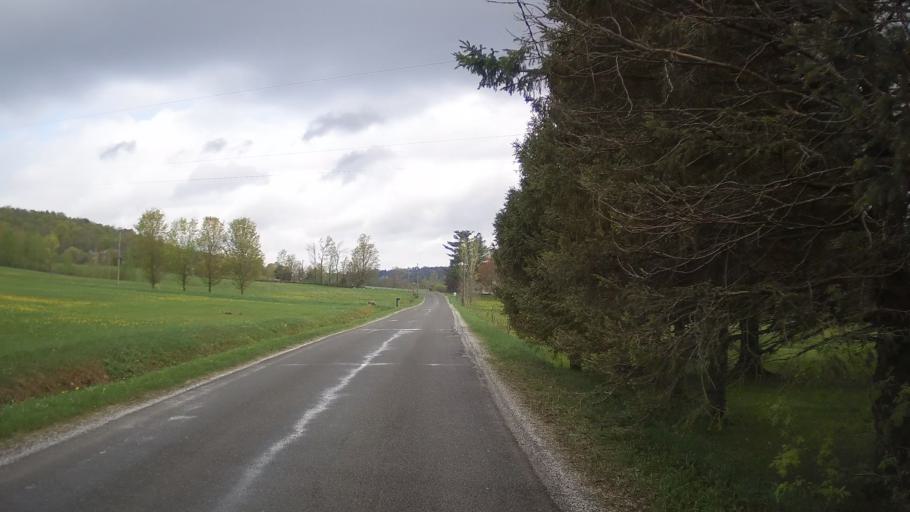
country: CA
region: Quebec
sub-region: Monteregie
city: Cowansville
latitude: 45.1869
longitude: -72.6977
